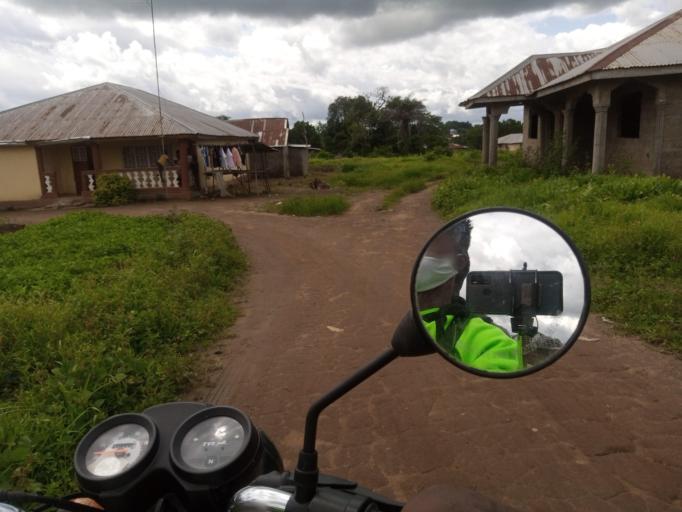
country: SL
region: Northern Province
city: Port Loko
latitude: 8.7759
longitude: -12.7741
